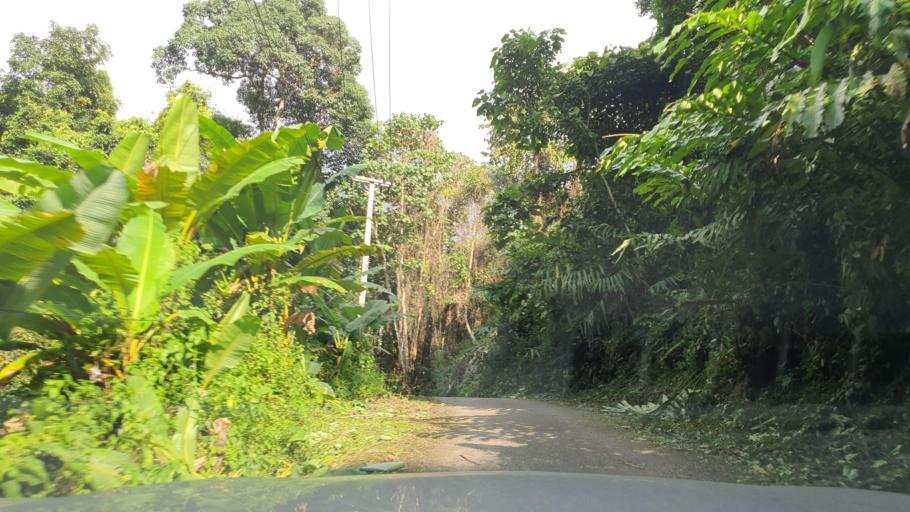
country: TH
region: Chiang Mai
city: Mae On
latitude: 18.9237
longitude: 99.3158
